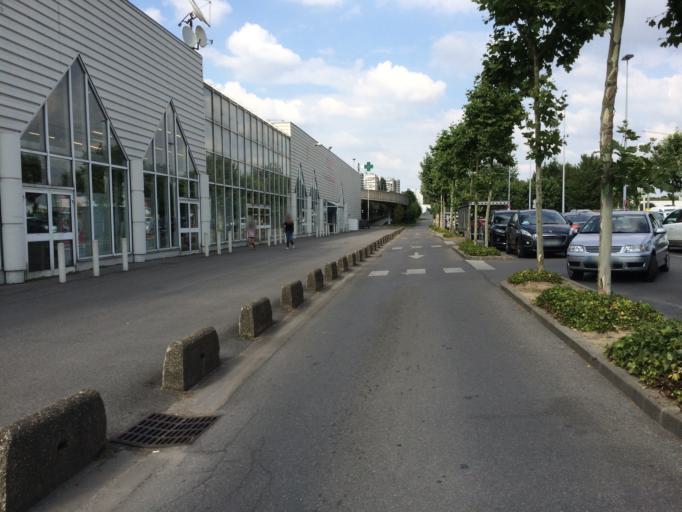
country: FR
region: Ile-de-France
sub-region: Departement de l'Essonne
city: Massy
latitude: 48.7239
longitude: 2.2775
